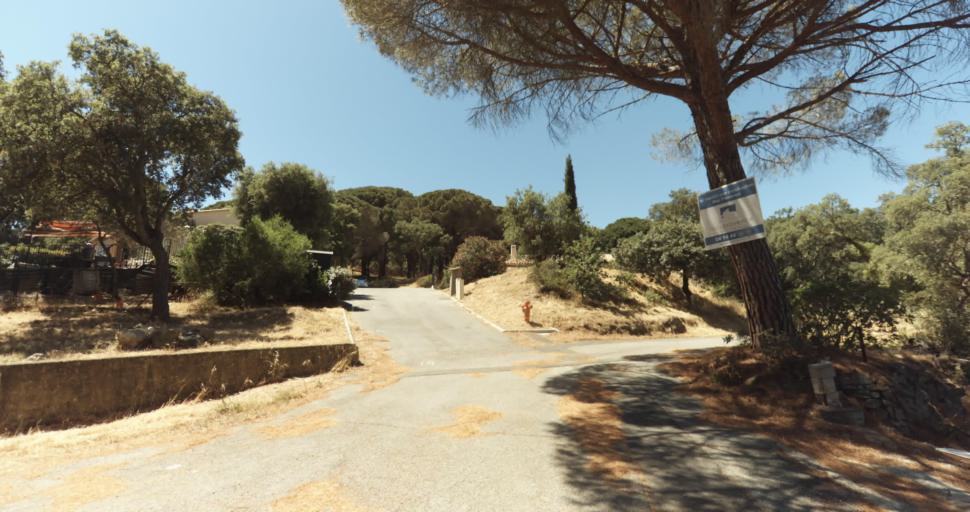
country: FR
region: Provence-Alpes-Cote d'Azur
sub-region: Departement du Var
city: Gassin
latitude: 43.2434
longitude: 6.5639
